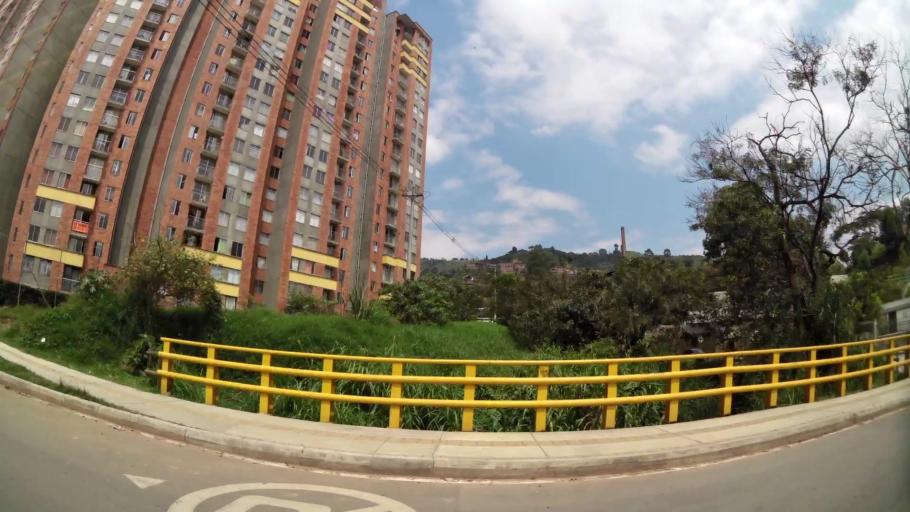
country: CO
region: Antioquia
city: Itagui
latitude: 6.1902
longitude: -75.6020
